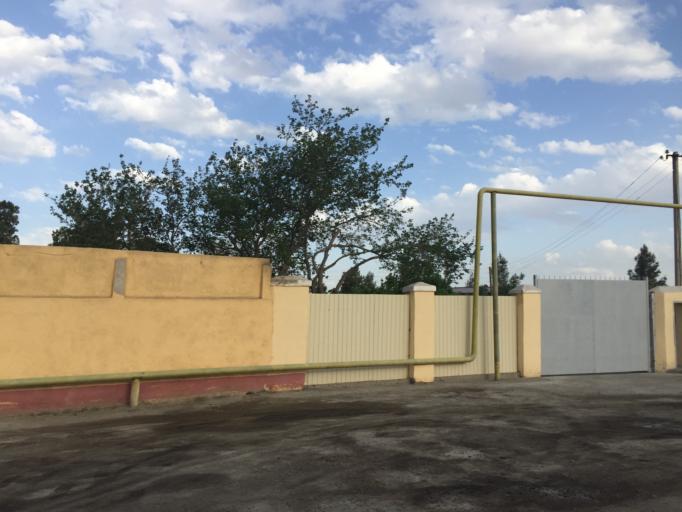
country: UZ
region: Bukhara
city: Kogon
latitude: 39.7314
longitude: 64.5630
